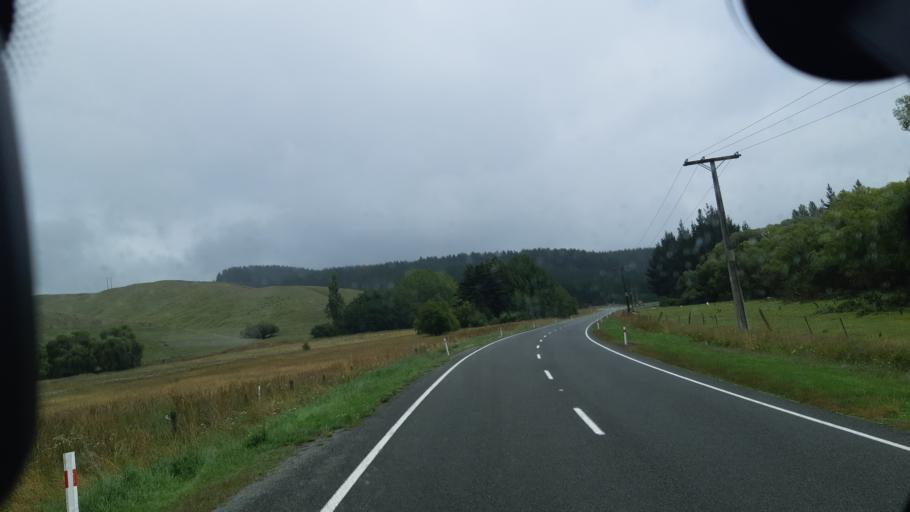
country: NZ
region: Canterbury
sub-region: Timaru District
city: Pleasant Point
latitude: -44.3097
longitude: 170.9505
